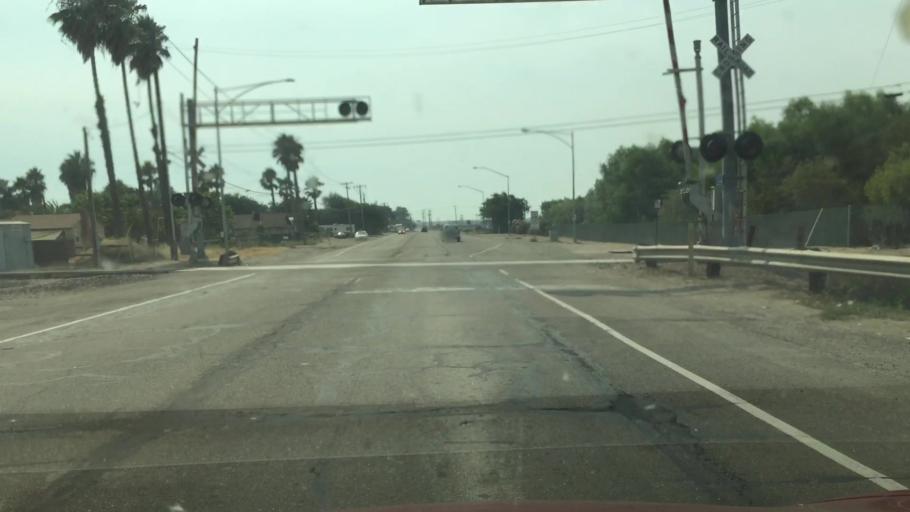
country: US
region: California
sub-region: San Joaquin County
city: Lathrop
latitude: 37.7973
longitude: -121.2637
